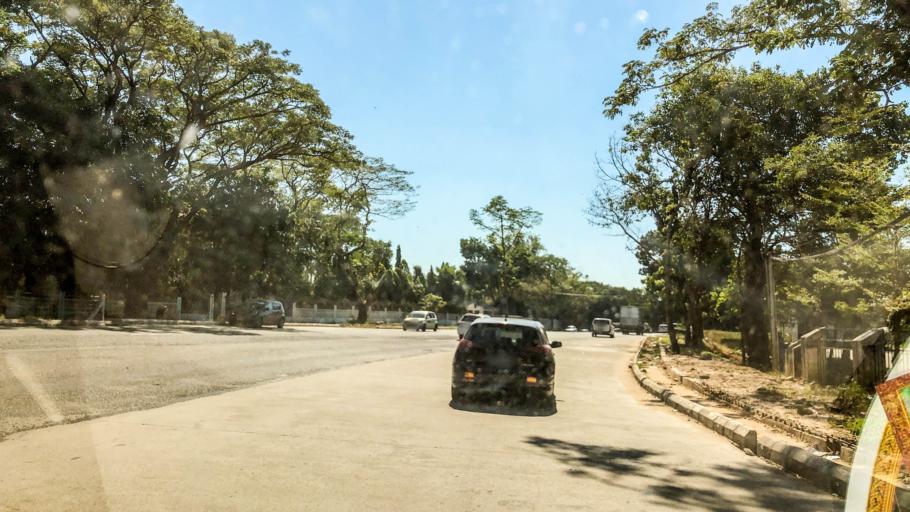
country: MM
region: Yangon
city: Yangon
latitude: 16.8964
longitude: 96.1315
